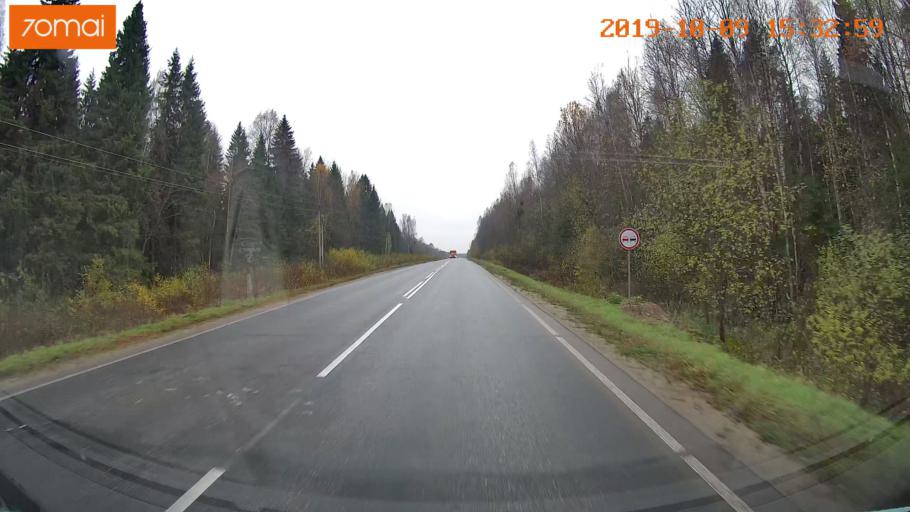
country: RU
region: Kostroma
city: Oktyabr'skiy
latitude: 57.9579
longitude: 41.2686
